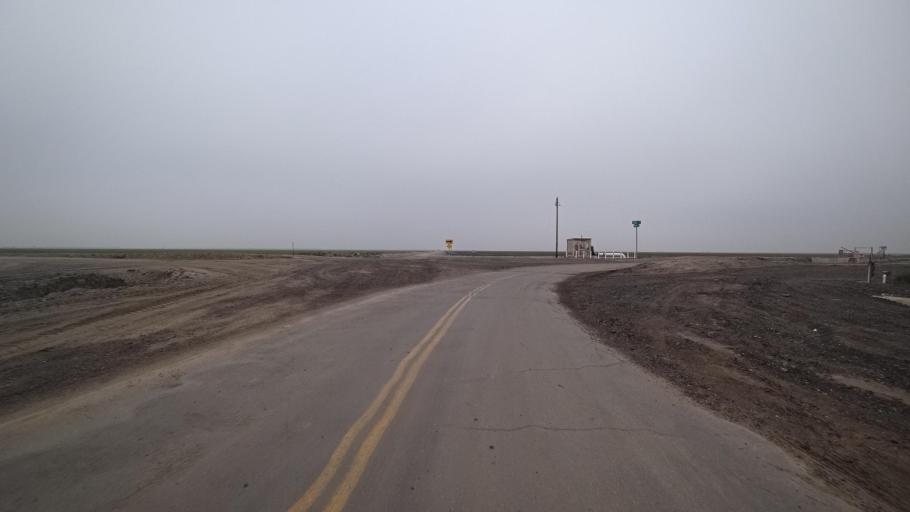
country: US
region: California
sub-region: Kern County
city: Rosedale
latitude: 35.1944
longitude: -119.1997
